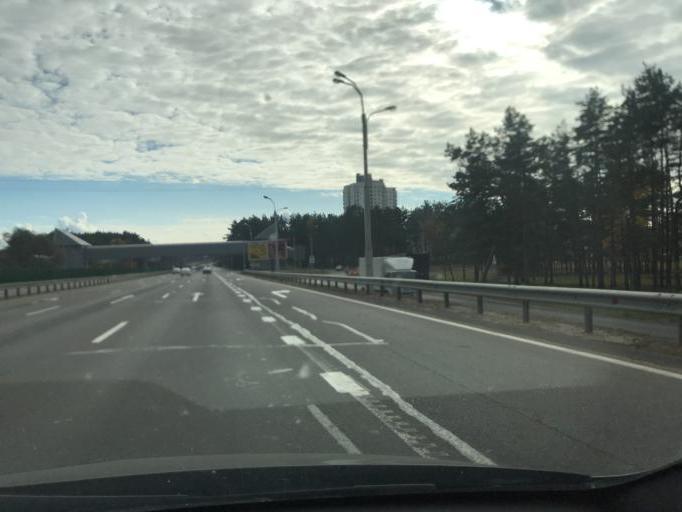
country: BY
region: Minsk
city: Vyaliki Trastsyanets
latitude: 53.8917
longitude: 27.6931
